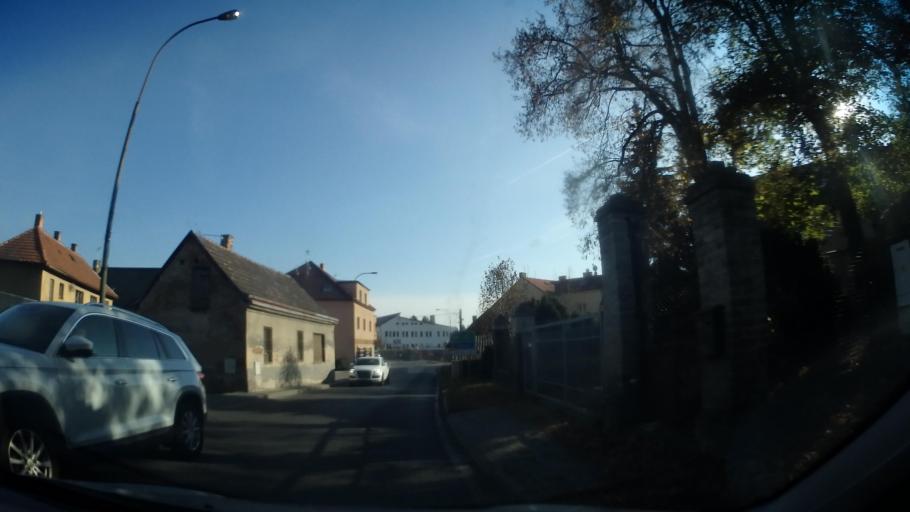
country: CZ
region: Central Bohemia
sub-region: Okres Praha-Vychod
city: Mnichovice
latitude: 49.9371
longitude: 14.7070
